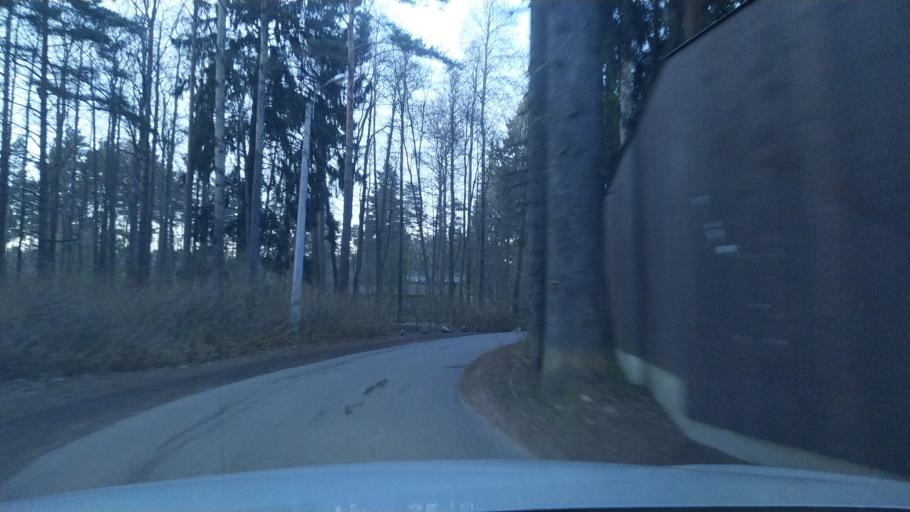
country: RU
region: St.-Petersburg
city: Solnechnoye
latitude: 60.1467
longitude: 29.9283
